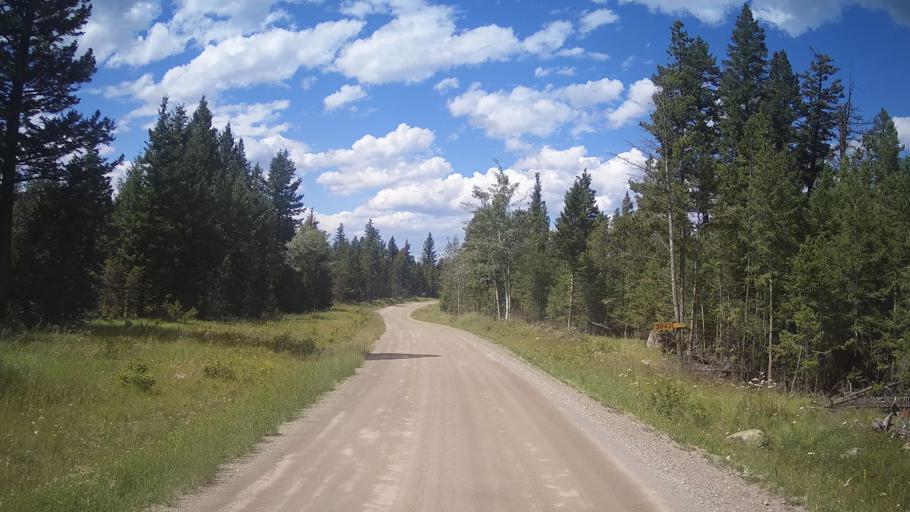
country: CA
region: British Columbia
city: Lillooet
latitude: 51.3163
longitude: -121.8586
